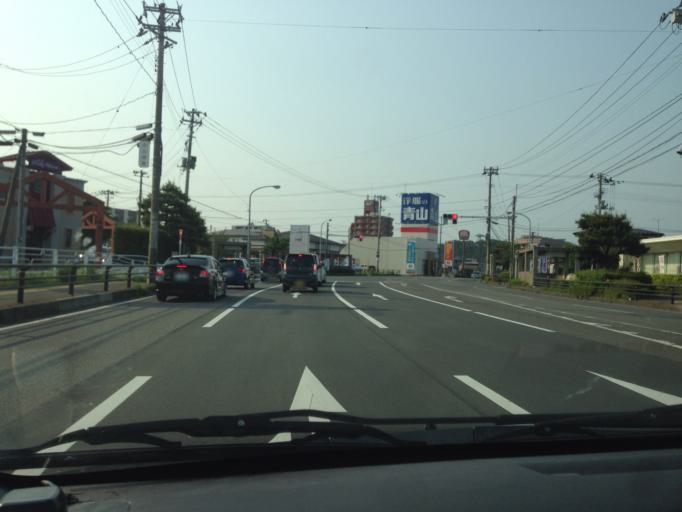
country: JP
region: Tochigi
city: Kuroiso
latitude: 37.1201
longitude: 140.1947
